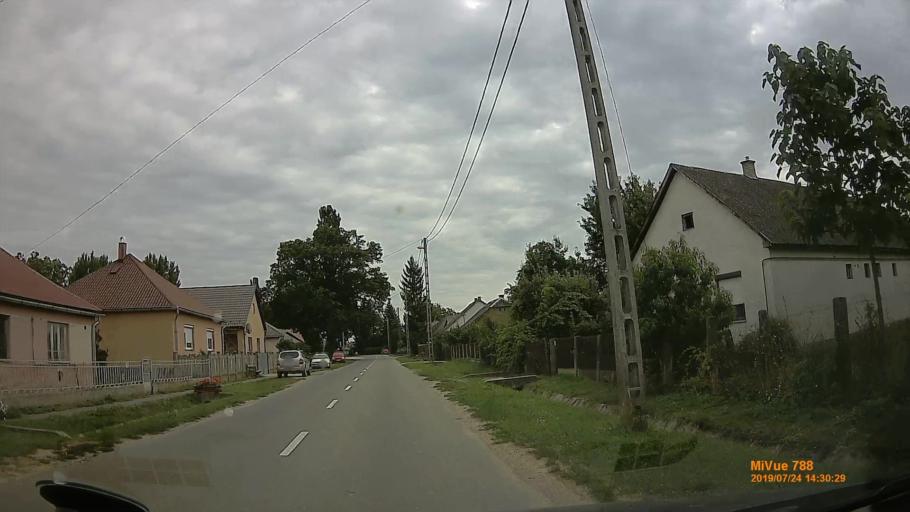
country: HU
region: Szabolcs-Szatmar-Bereg
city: Mandok
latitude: 48.3249
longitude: 22.2657
